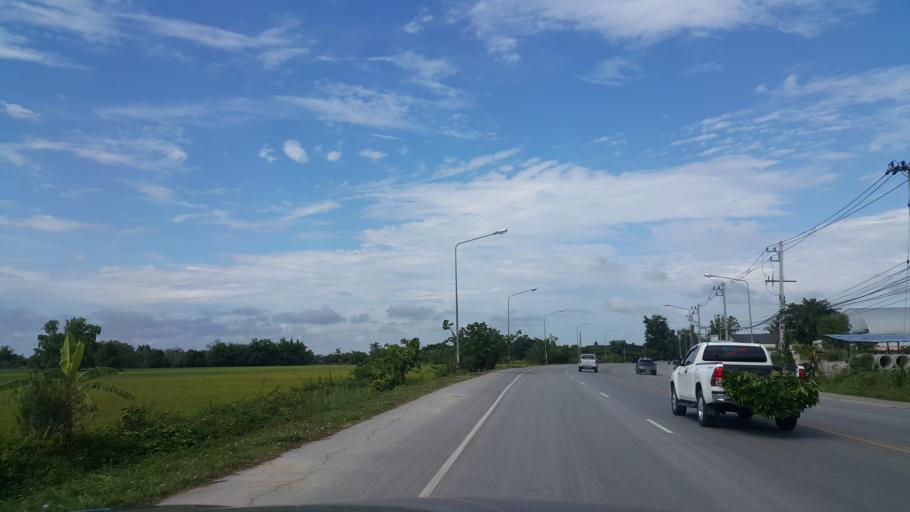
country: TH
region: Chiang Rai
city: Chiang Rai
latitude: 19.9123
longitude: 99.8649
